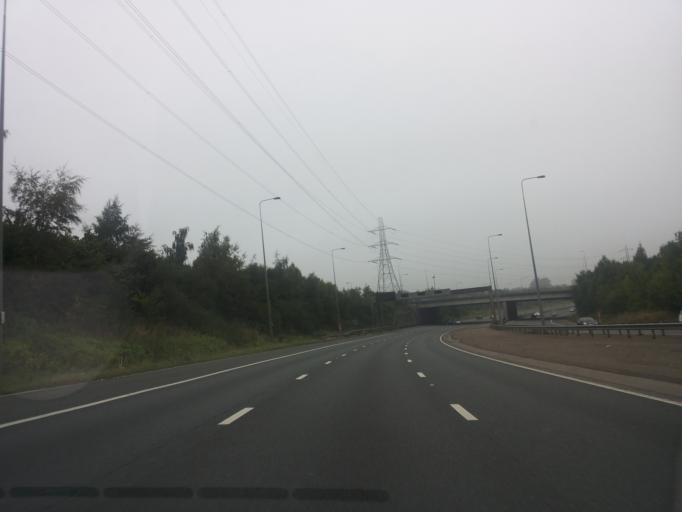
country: GB
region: England
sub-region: Borough of Rochdale
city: Middleton
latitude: 53.5327
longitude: -2.2045
